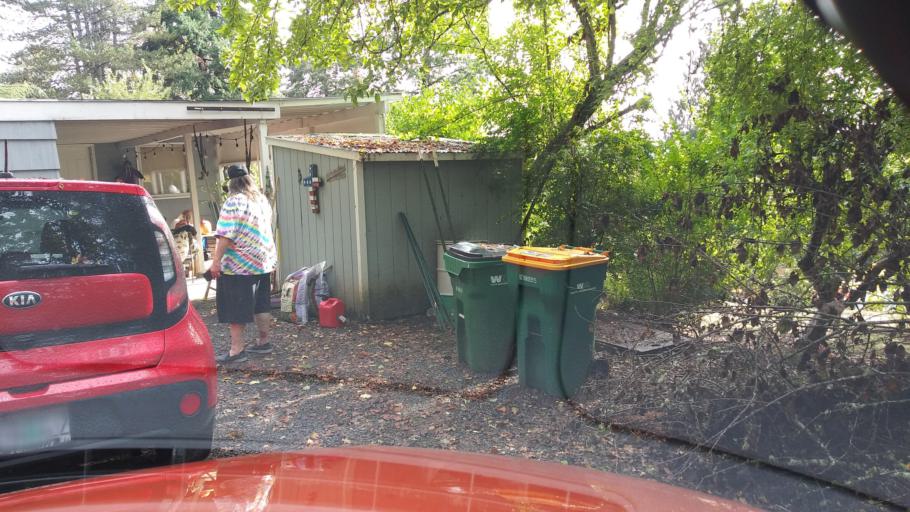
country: US
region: Oregon
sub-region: Washington County
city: Forest Grove
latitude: 45.5334
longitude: -123.1384
